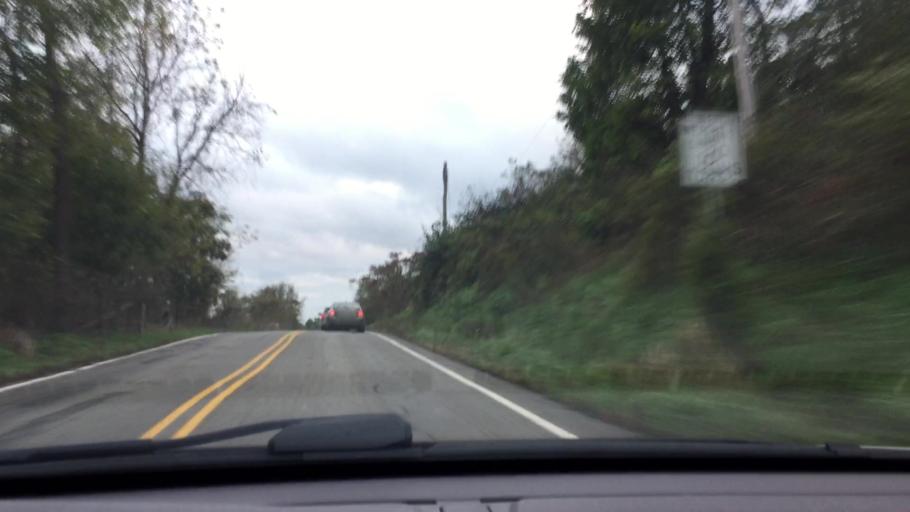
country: US
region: Pennsylvania
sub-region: Washington County
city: McMurray
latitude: 40.1981
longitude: -80.1191
